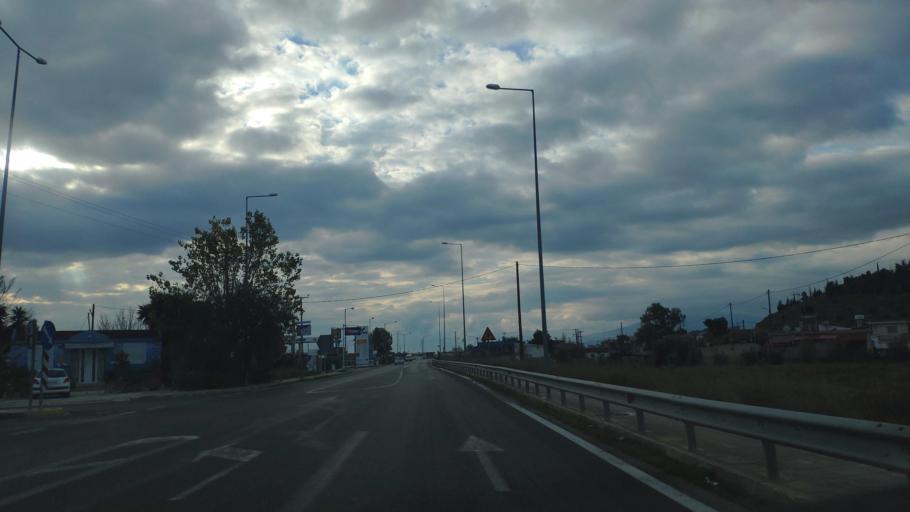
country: GR
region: Peloponnese
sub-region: Nomos Argolidos
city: Argos
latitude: 37.6497
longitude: 22.7289
